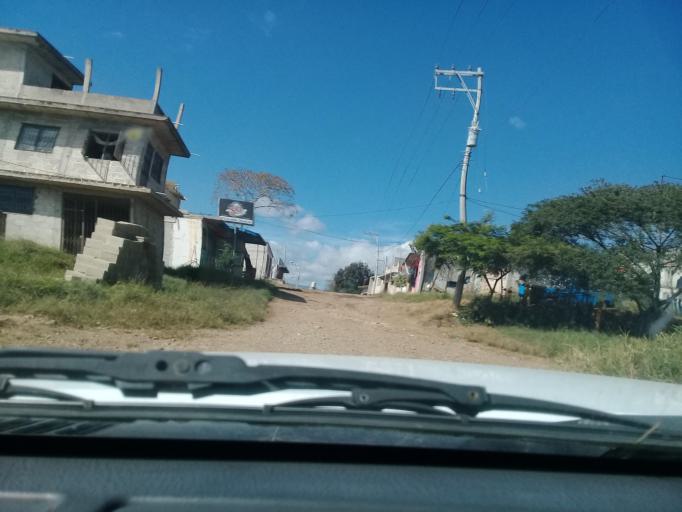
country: MX
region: Veracruz
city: El Castillo
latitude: 19.5650
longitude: -96.8795
